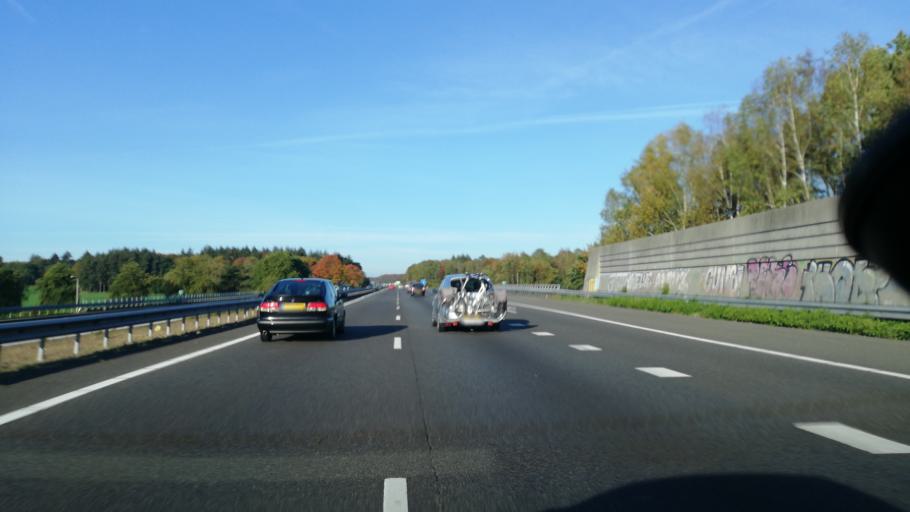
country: NL
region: Gelderland
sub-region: Gemeente Apeldoorn
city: Beekbergen
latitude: 52.1820
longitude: 5.9168
